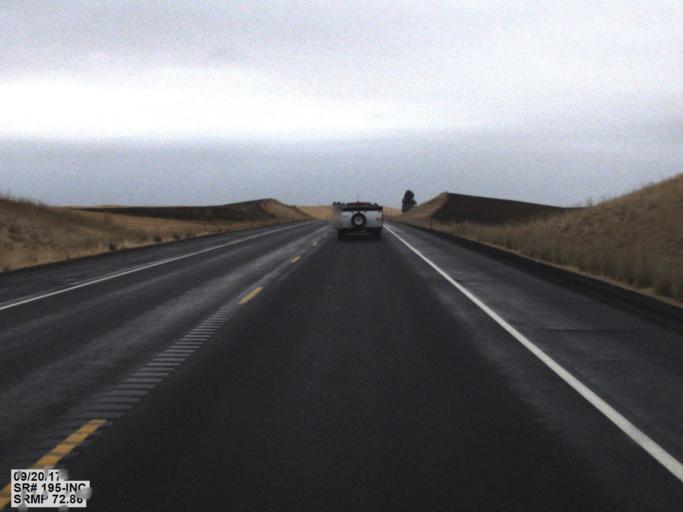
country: US
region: Washington
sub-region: Spokane County
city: Cheney
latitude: 47.3384
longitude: -117.3806
